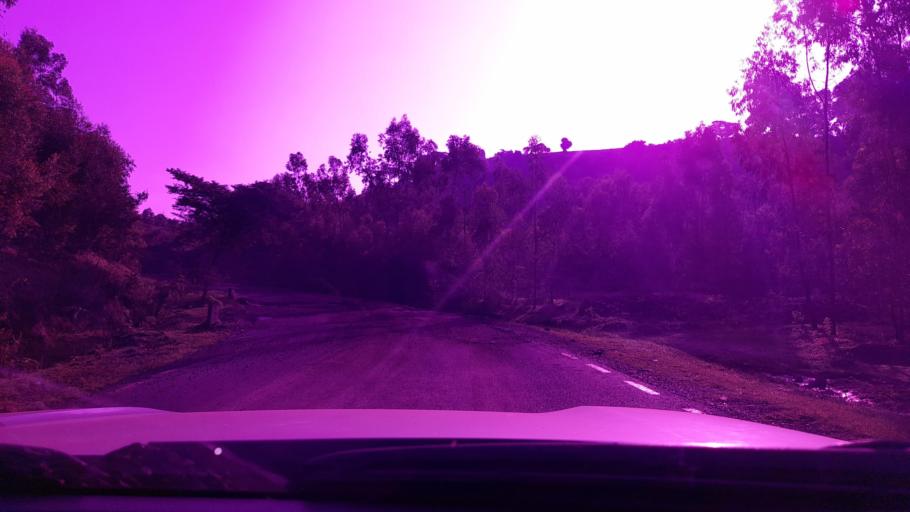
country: ET
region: Oromiya
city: Bedele
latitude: 8.1466
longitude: 36.4594
